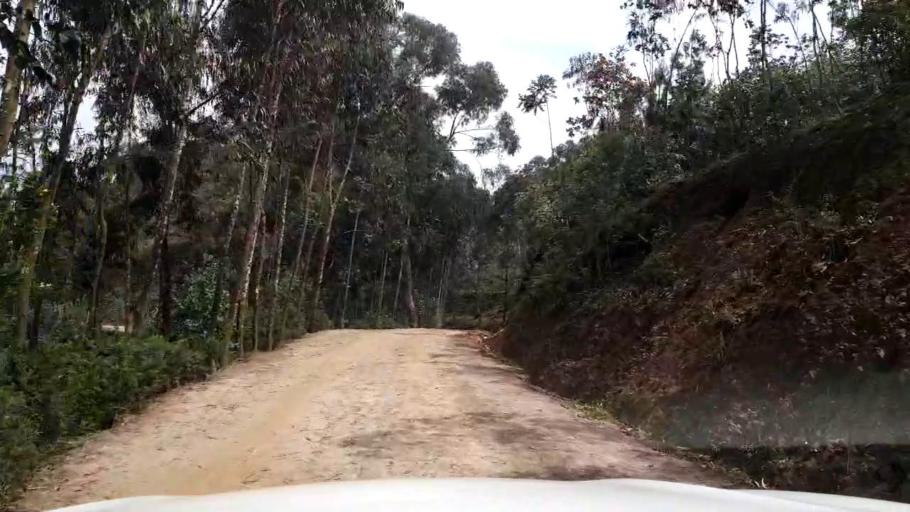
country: RW
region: Western Province
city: Kibuye
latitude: -1.9360
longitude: 29.4536
